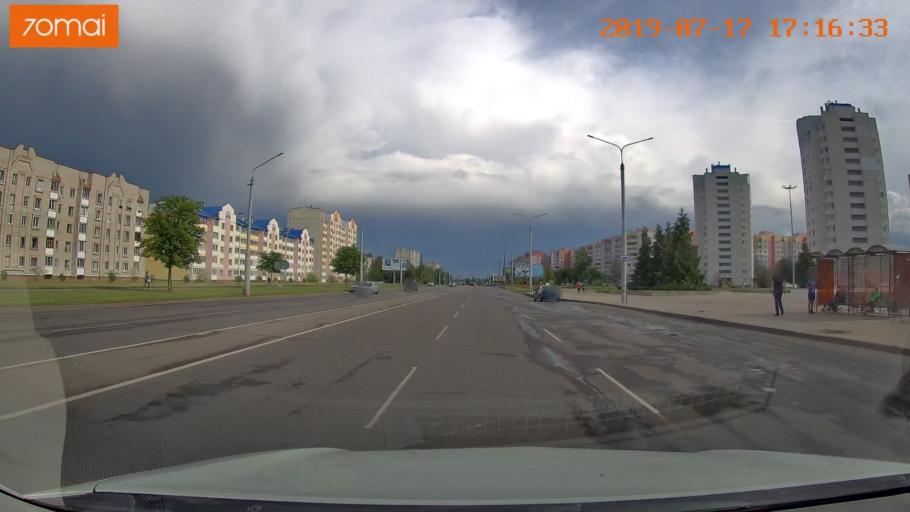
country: BY
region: Mogilev
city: Babruysk
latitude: 53.1672
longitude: 29.1938
